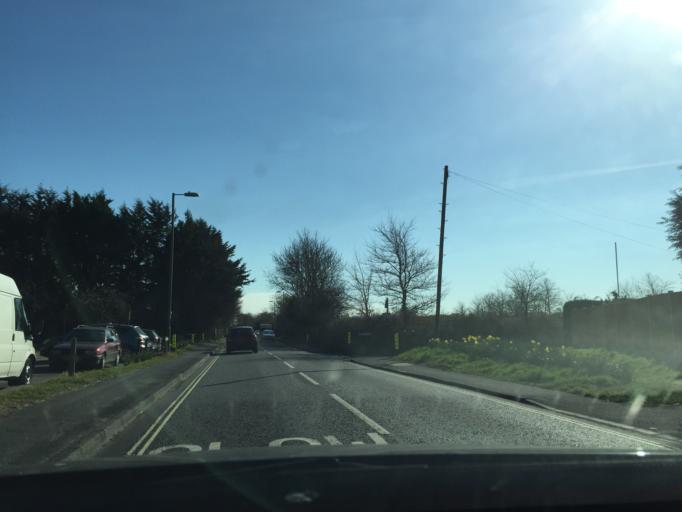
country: GB
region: England
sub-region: Hampshire
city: Hayling Island
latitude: 50.8102
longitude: -0.9771
